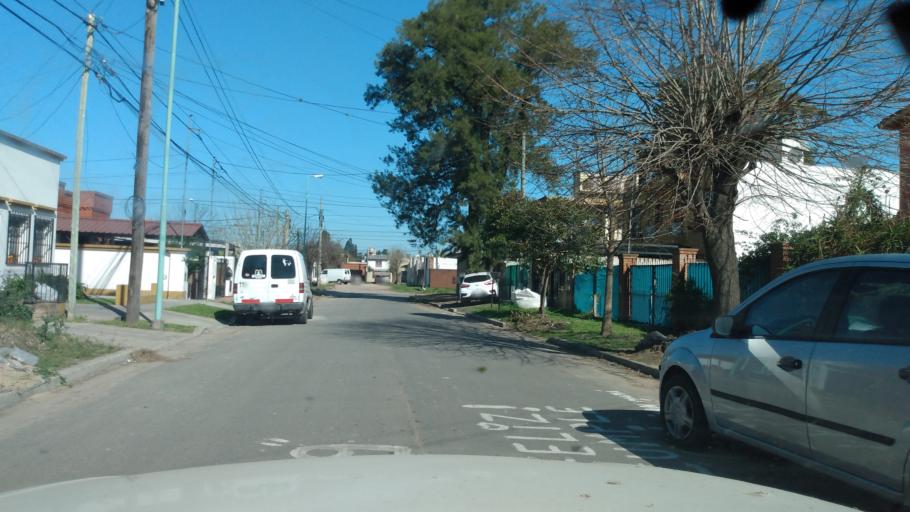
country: AR
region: Buenos Aires
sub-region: Partido de Lujan
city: Lujan
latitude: -34.5688
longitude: -59.0932
